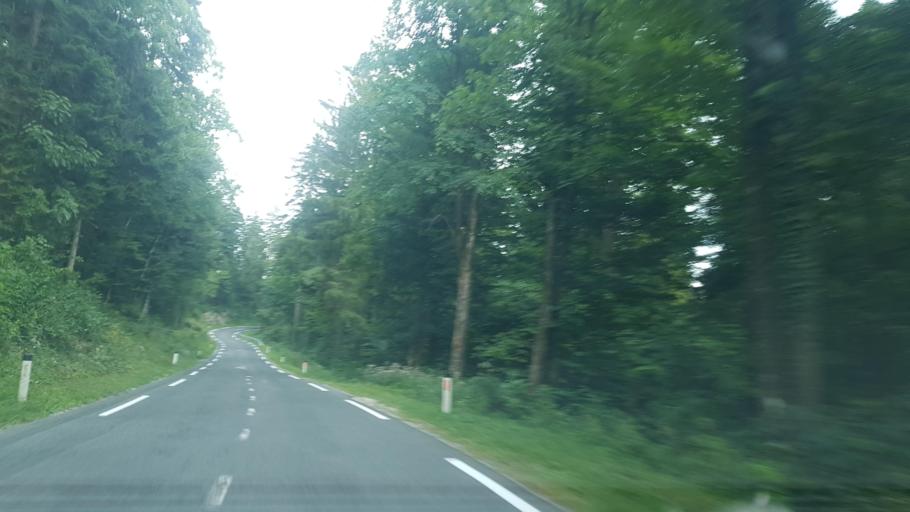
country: SI
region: Logatec
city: Logatec
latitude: 45.8733
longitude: 14.1335
